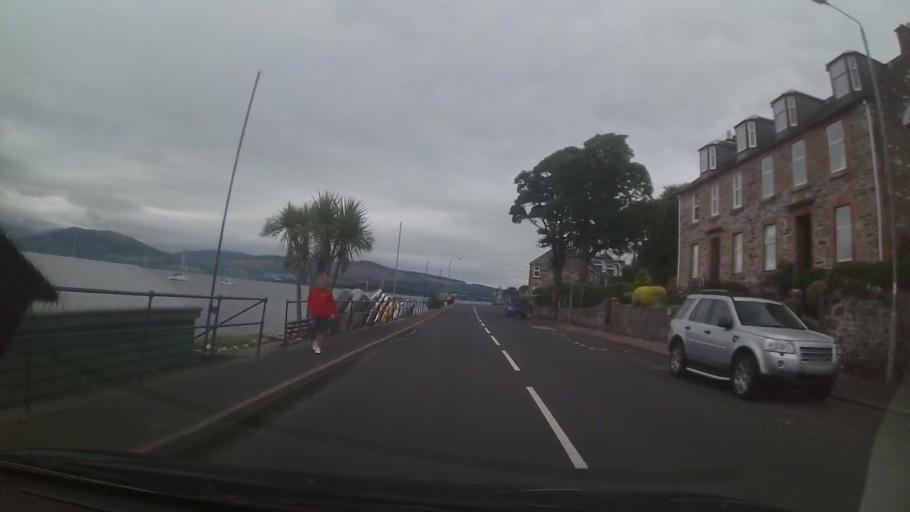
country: GB
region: Scotland
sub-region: Argyll and Bute
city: Port Bannatyne
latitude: 55.8602
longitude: -5.0801
